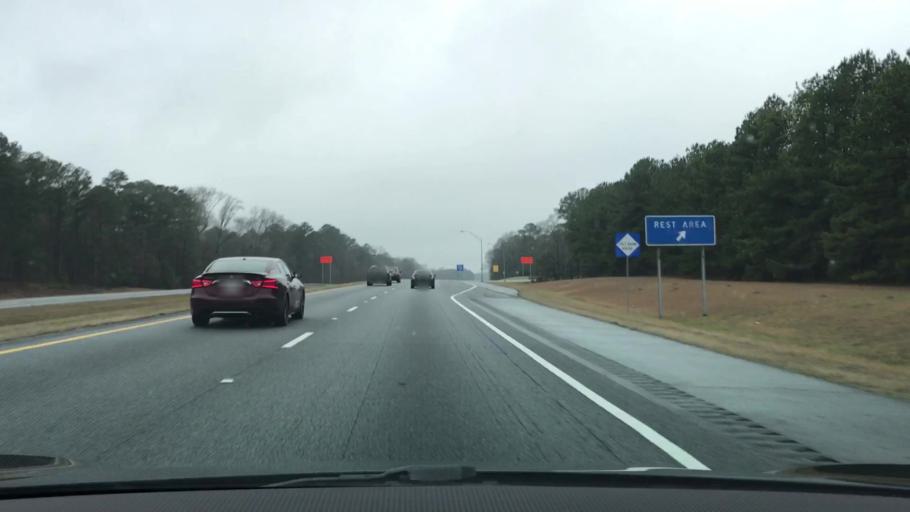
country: US
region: Georgia
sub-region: Morgan County
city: Madison
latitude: 33.5772
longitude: -83.5726
